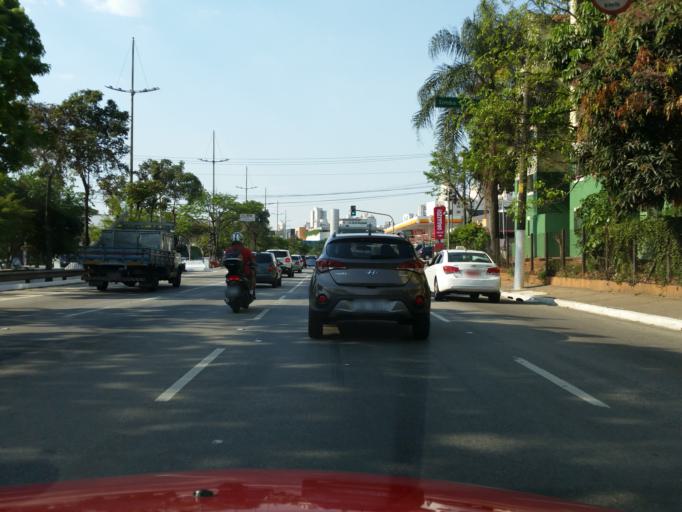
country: BR
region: Sao Paulo
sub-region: Diadema
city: Diadema
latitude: -23.6260
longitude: -46.6290
